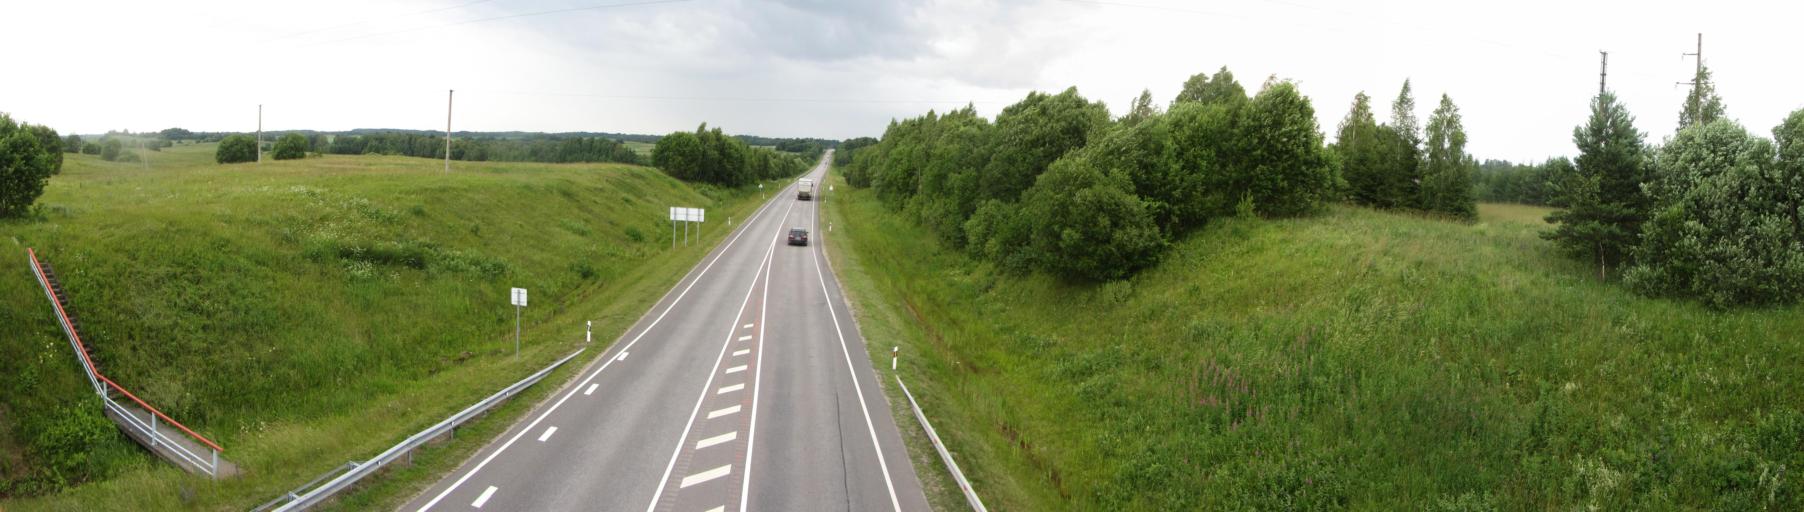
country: LT
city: Moletai
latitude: 55.0635
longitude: 25.3502
